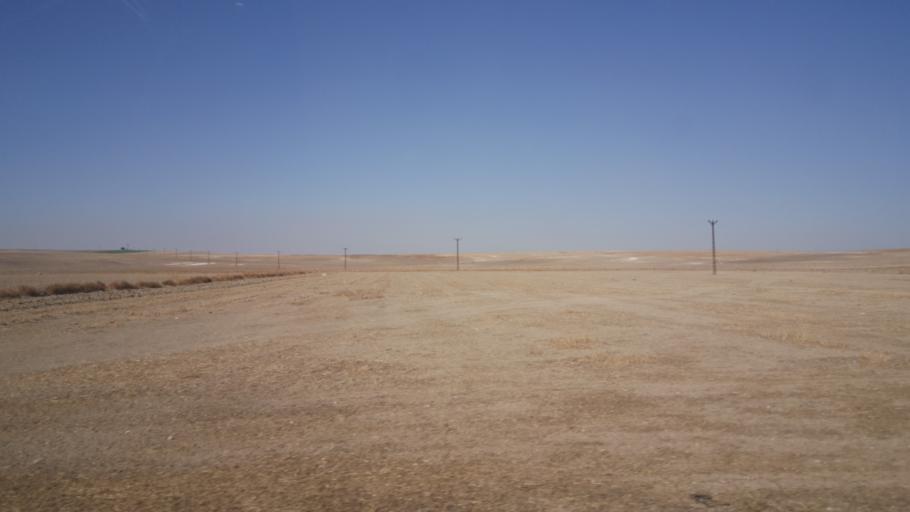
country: TR
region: Konya
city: Celtik
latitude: 39.0613
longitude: 31.8595
